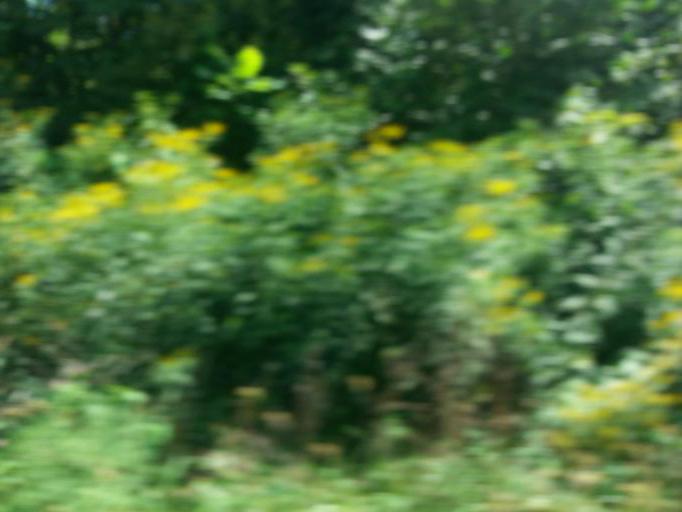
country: US
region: Virginia
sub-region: Washington County
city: Abingdon
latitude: 36.6631
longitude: -82.0705
